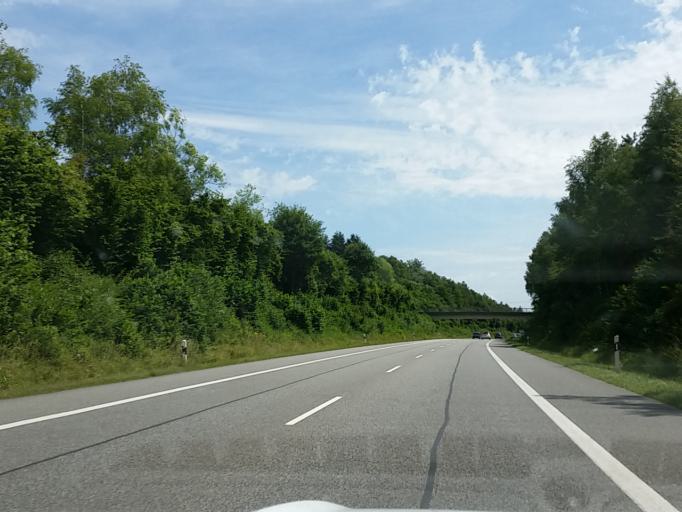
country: DE
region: Saarland
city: Losheim
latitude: 49.5119
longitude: 6.7744
